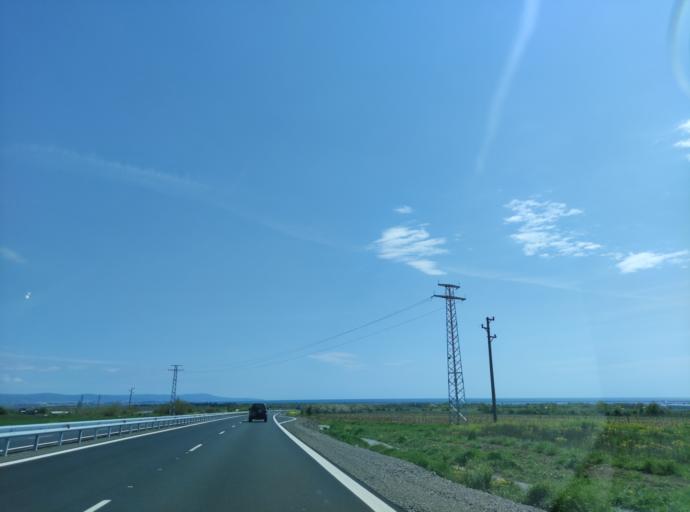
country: BG
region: Burgas
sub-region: Obshtina Pomorie
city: Pomorie
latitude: 42.5866
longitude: 27.5916
